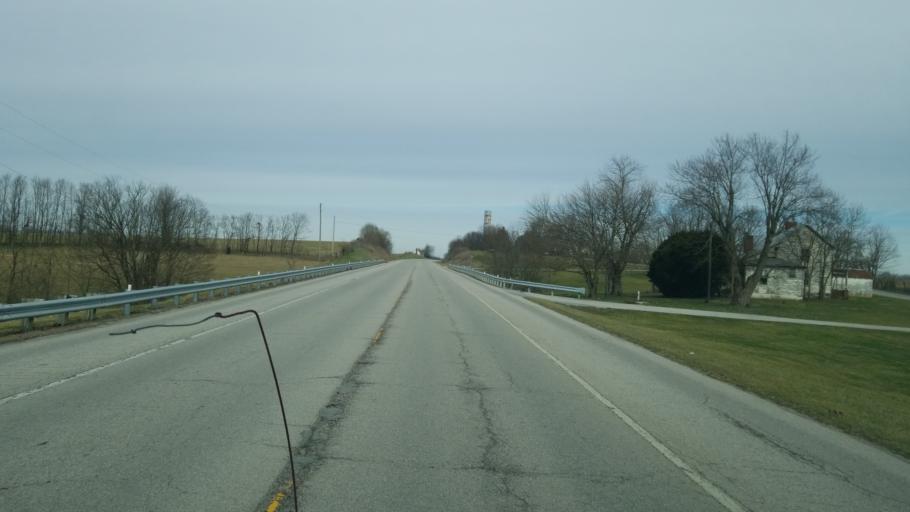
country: US
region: Kentucky
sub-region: Fleming County
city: Flemingsburg
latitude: 38.4995
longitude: -83.8526
